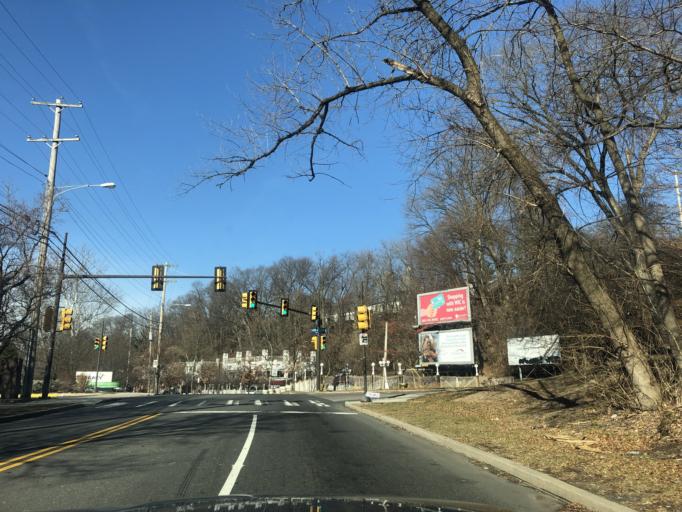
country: US
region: Pennsylvania
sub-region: Montgomery County
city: Bala-Cynwyd
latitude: 40.0128
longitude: -75.2017
